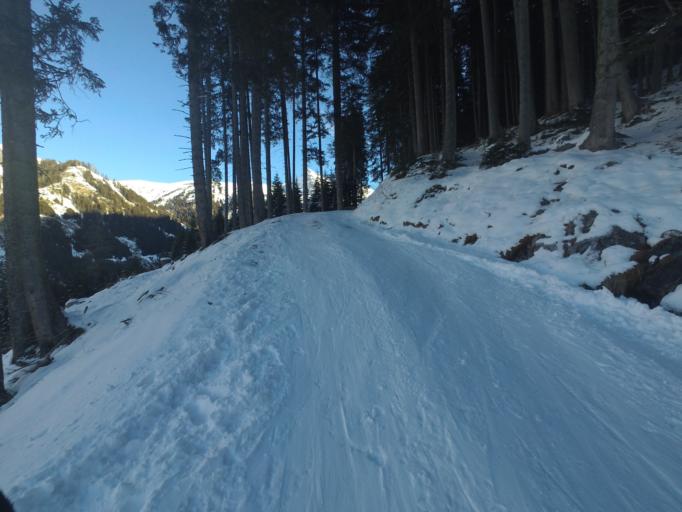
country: AT
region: Salzburg
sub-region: Politischer Bezirk Sankt Johann im Pongau
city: Huttschlag
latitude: 47.1798
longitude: 13.2750
